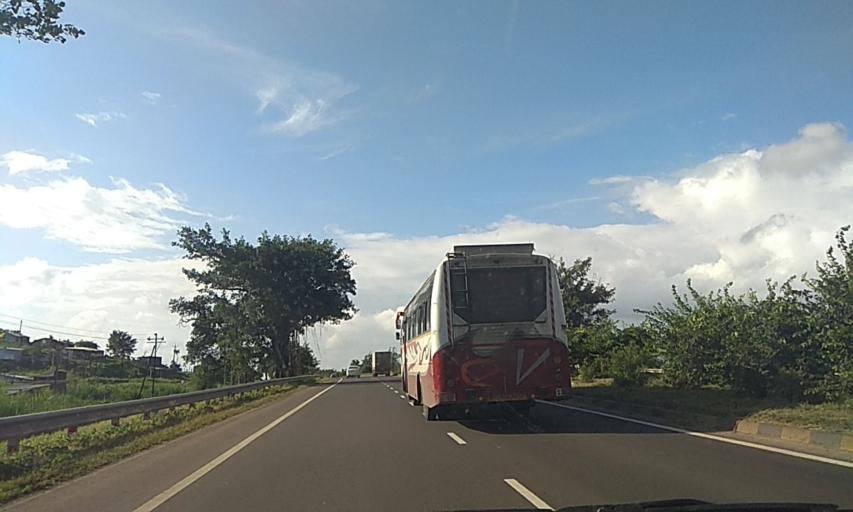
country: IN
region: Maharashtra
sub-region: Satara Division
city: Karad
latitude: 17.3298
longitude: 74.1459
